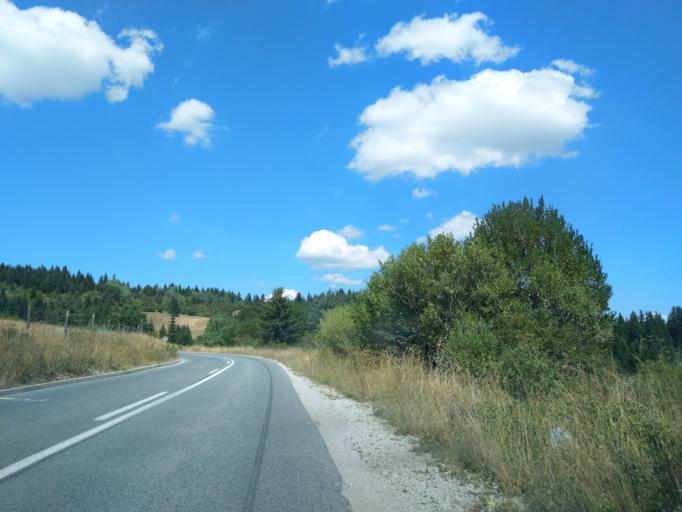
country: RS
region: Central Serbia
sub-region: Zlatiborski Okrug
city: Nova Varos
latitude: 43.3910
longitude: 19.8476
